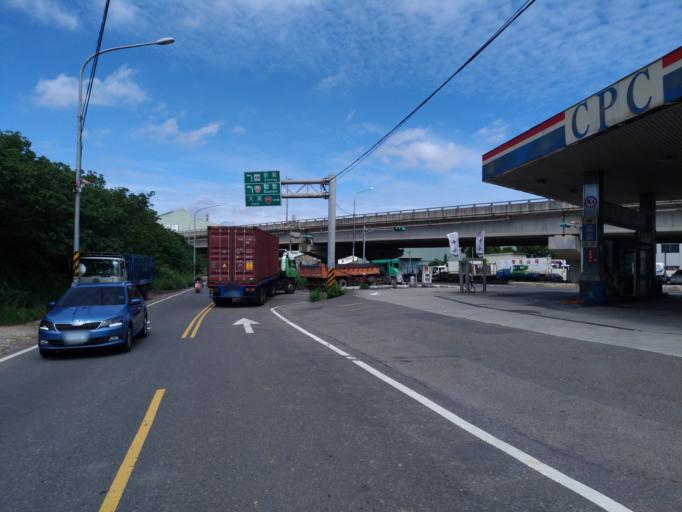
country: TW
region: Taiwan
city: Taoyuan City
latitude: 24.9472
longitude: 121.1652
